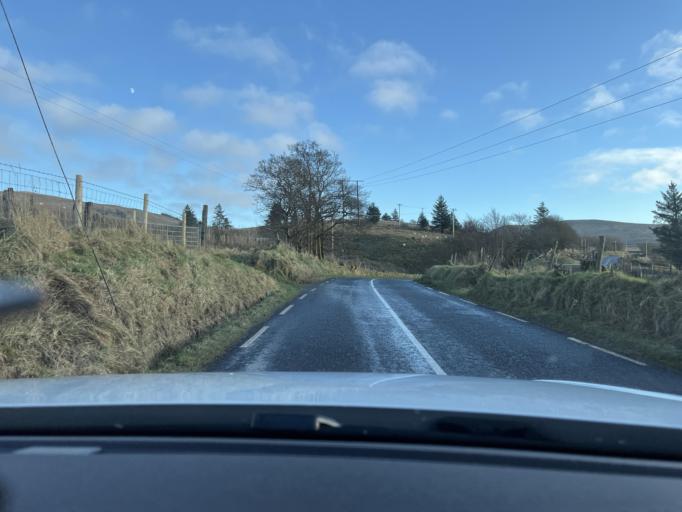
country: GB
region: Northern Ireland
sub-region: Fermanagh District
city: Enniskillen
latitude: 54.1769
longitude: -7.8523
